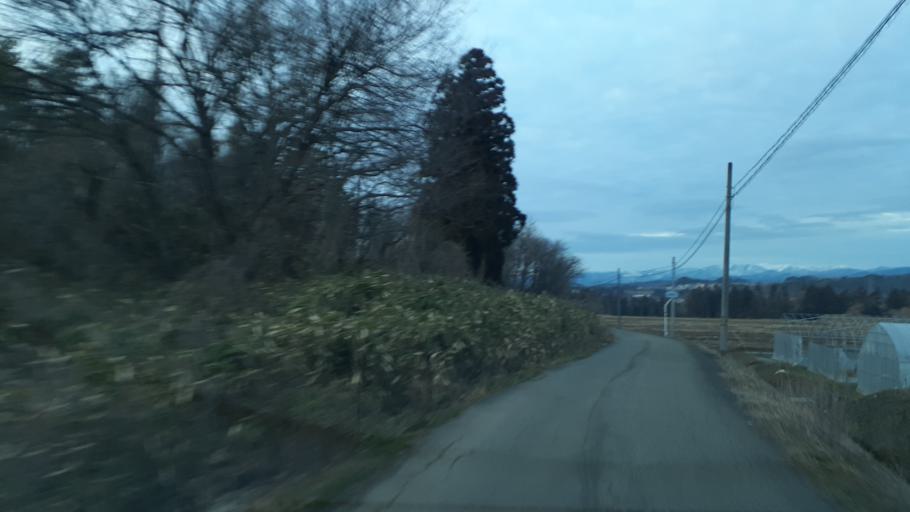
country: JP
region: Fukushima
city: Kitakata
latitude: 37.5348
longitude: 139.9483
